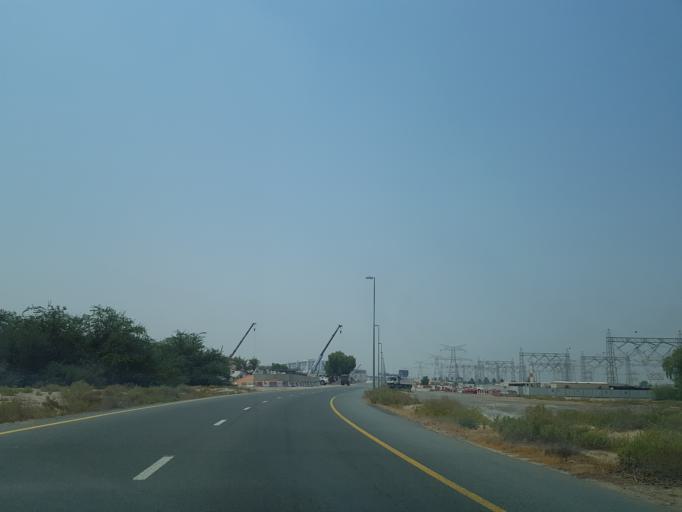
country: AE
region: Ash Shariqah
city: Sharjah
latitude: 25.2277
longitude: 55.4099
